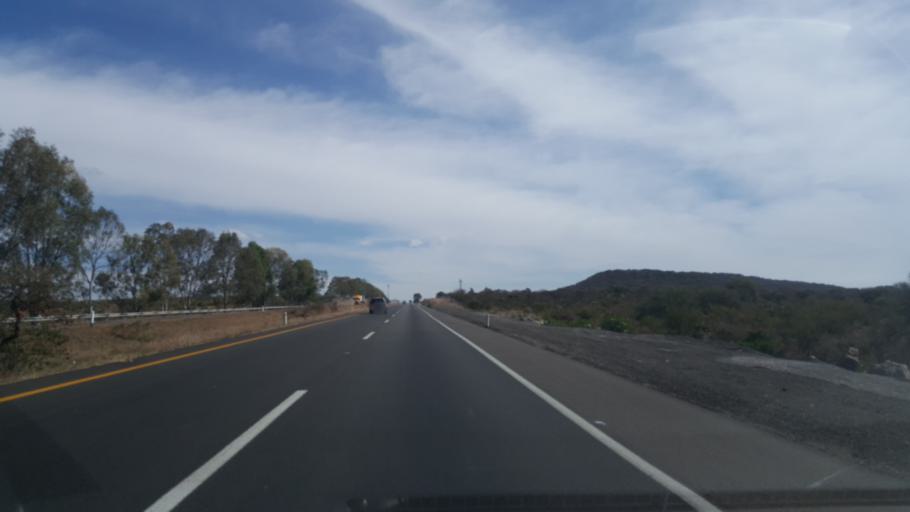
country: MX
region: Jalisco
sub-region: Lagos de Moreno
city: Cristeros [Fraccionamiento]
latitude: 21.2687
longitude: -101.9701
